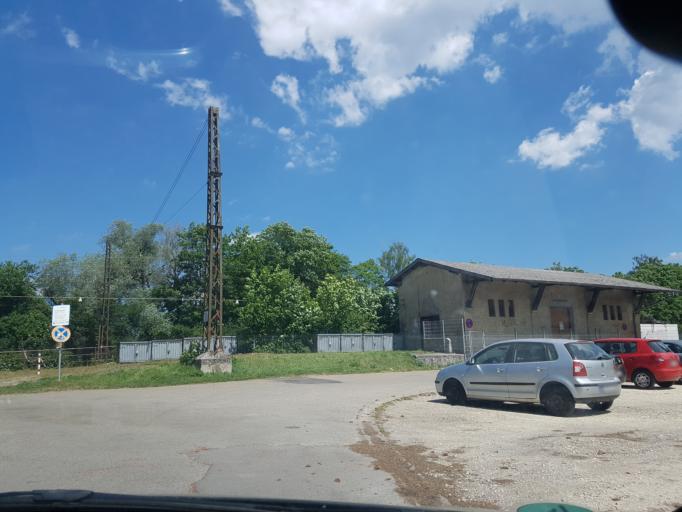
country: DE
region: Bavaria
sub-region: Swabia
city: Nersingen
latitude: 48.4300
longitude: 10.1186
